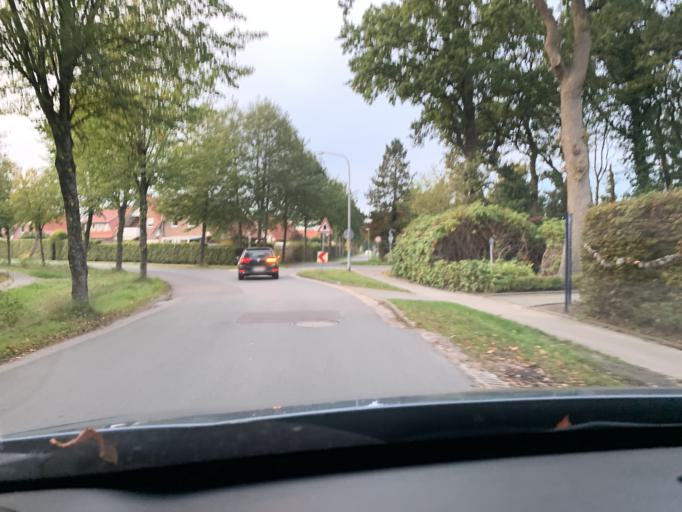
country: DE
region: Lower Saxony
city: Westerstede
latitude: 53.2544
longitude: 7.9034
